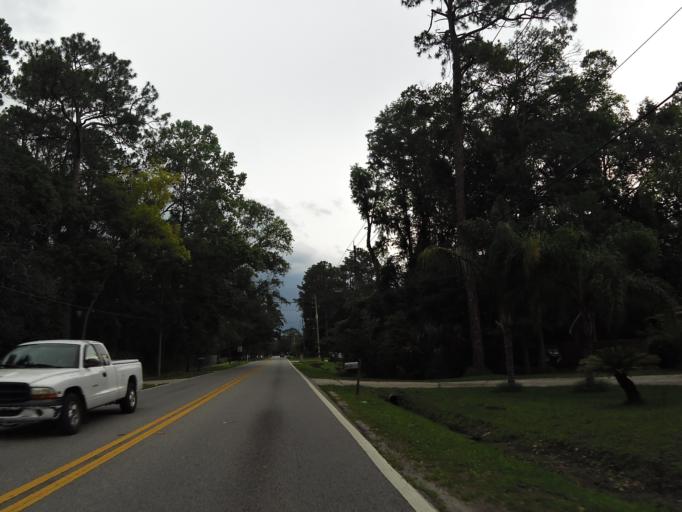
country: US
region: Florida
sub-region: Duval County
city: Jacksonville
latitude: 30.2818
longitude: -81.5829
